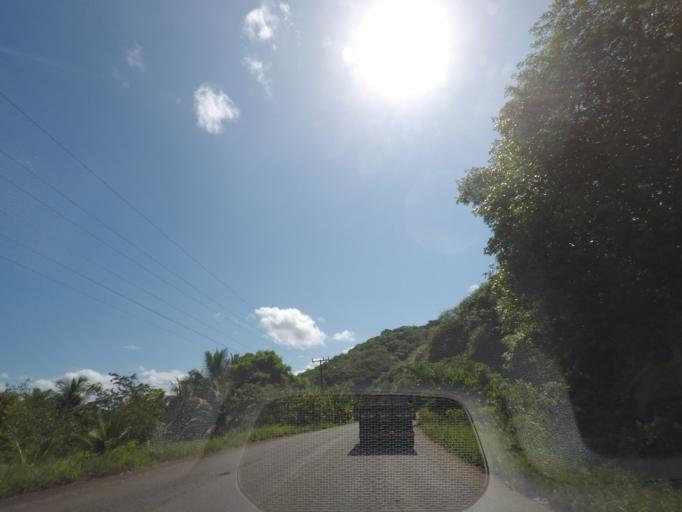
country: BR
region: Bahia
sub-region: Itubera
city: Itubera
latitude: -13.7022
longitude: -39.1360
